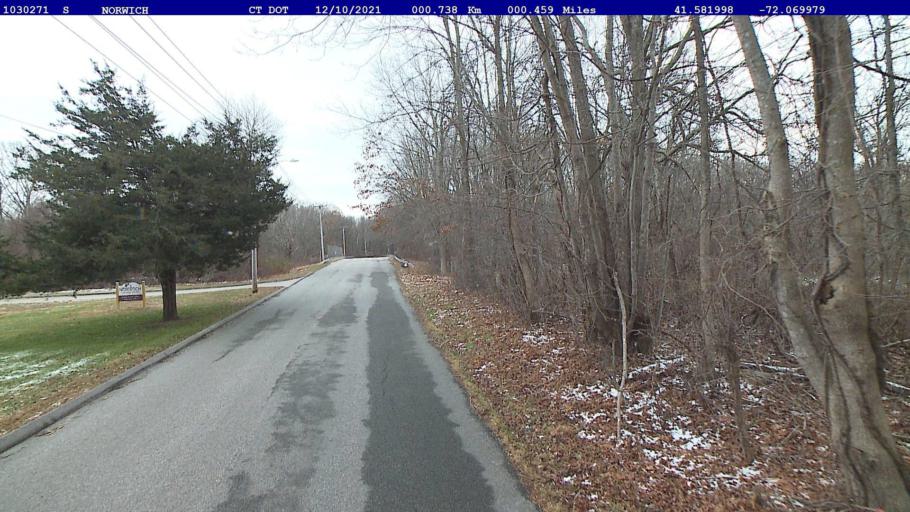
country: US
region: Connecticut
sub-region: New London County
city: Baltic
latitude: 41.5820
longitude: -72.0700
